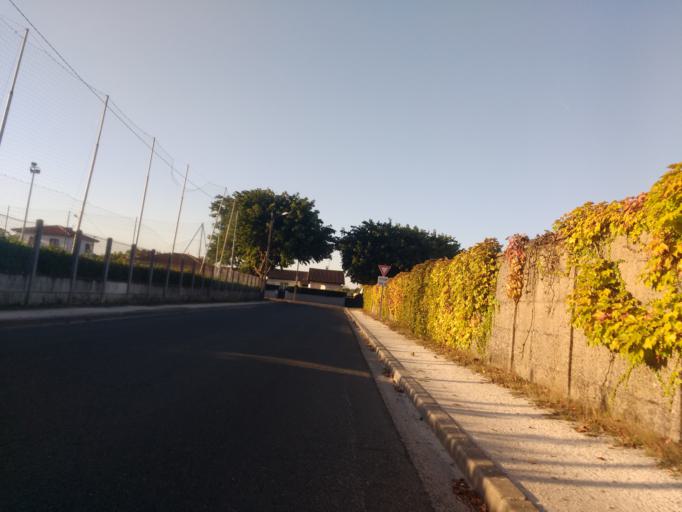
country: FR
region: Aquitaine
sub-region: Departement de la Gironde
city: Pessac
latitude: 44.8127
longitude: -0.6276
